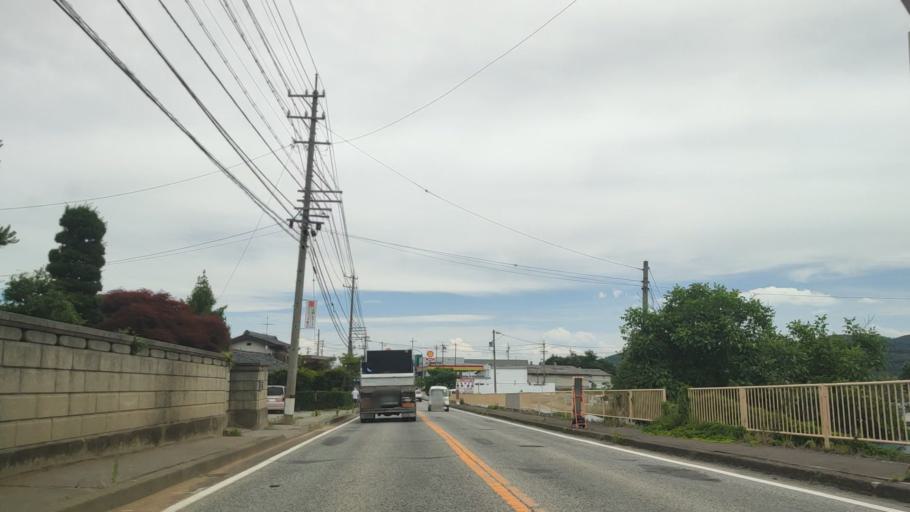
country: JP
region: Nagano
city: Komoro
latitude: 36.3416
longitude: 138.3885
